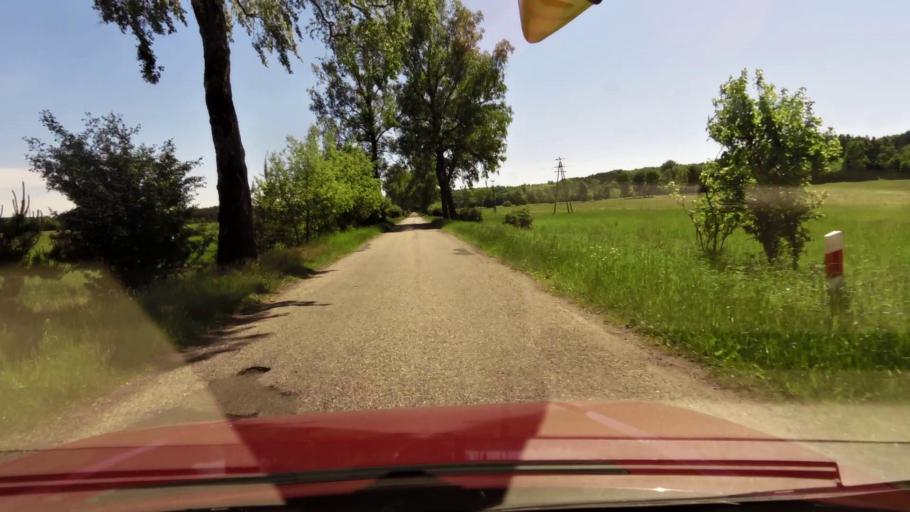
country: PL
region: West Pomeranian Voivodeship
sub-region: Powiat koszalinski
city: Bobolice
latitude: 54.0387
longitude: 16.6024
